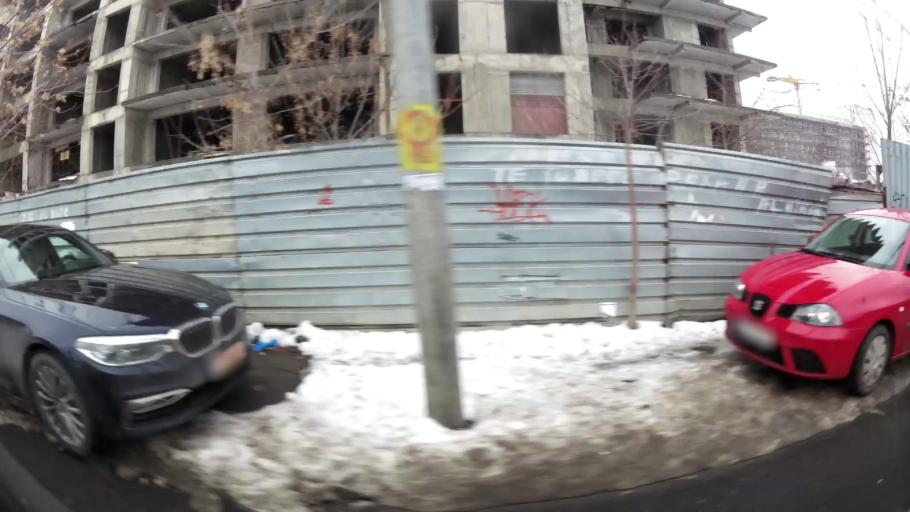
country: RO
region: Bucuresti
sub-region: Municipiul Bucuresti
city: Bucharest
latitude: 44.4133
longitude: 26.1262
